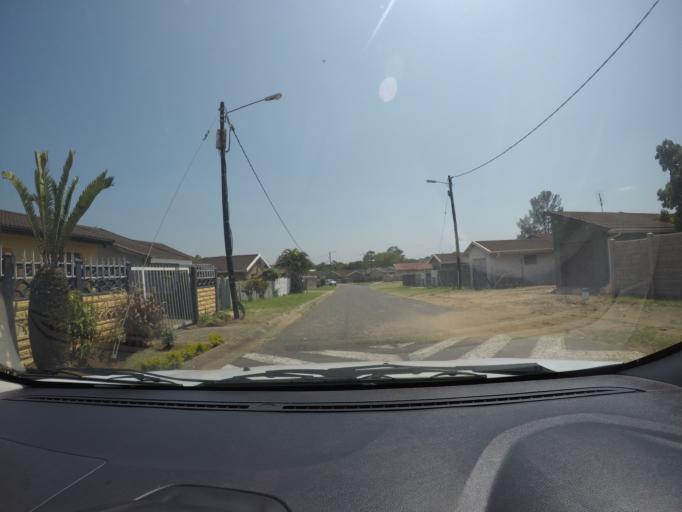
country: ZA
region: KwaZulu-Natal
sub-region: uThungulu District Municipality
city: eSikhawini
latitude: -28.8685
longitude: 31.9254
